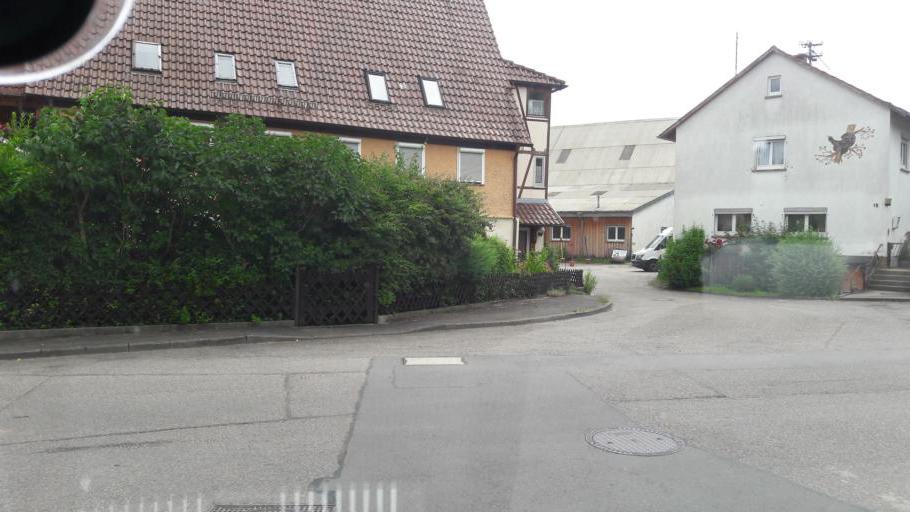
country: DE
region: Baden-Wuerttemberg
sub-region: Regierungsbezirk Stuttgart
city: Ohringen
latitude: 49.1982
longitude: 9.5268
